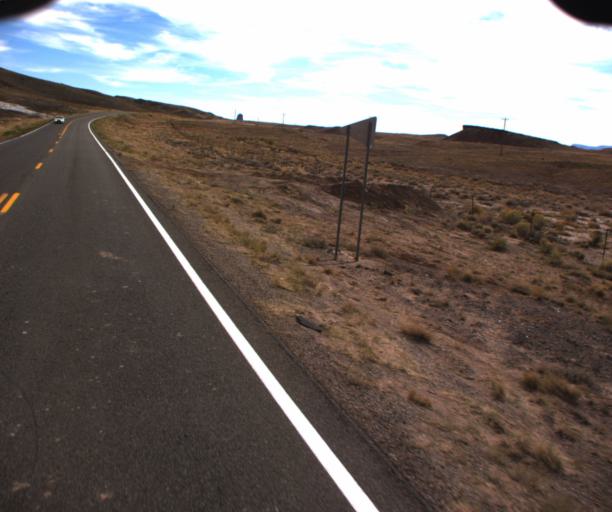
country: US
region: Arizona
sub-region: Navajo County
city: Kayenta
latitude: 36.8279
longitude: -110.2407
